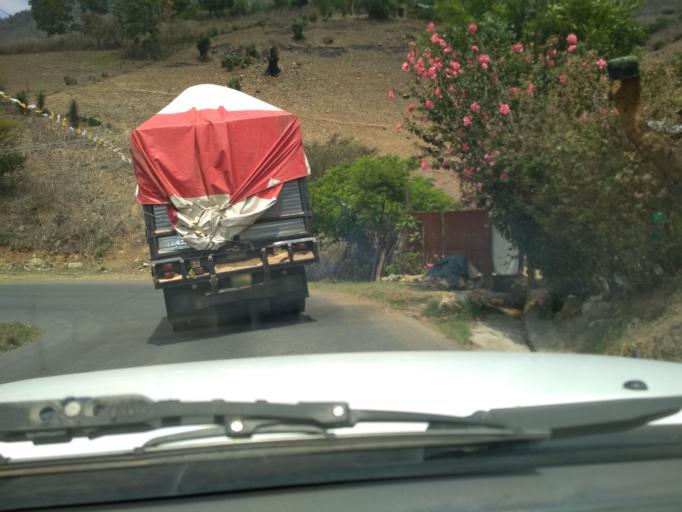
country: MX
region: Veracruz
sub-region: Acultzingo
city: Acatla
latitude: 18.7535
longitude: -97.1959
